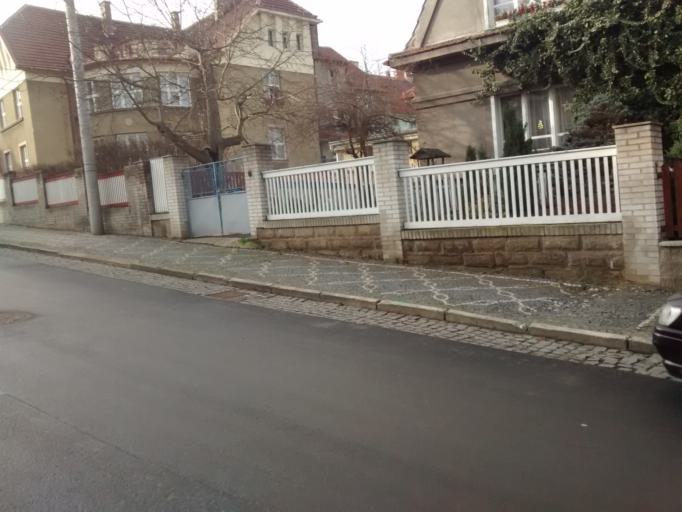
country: CZ
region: Ustecky
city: Roudnice nad Labem
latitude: 50.4248
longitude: 14.2533
